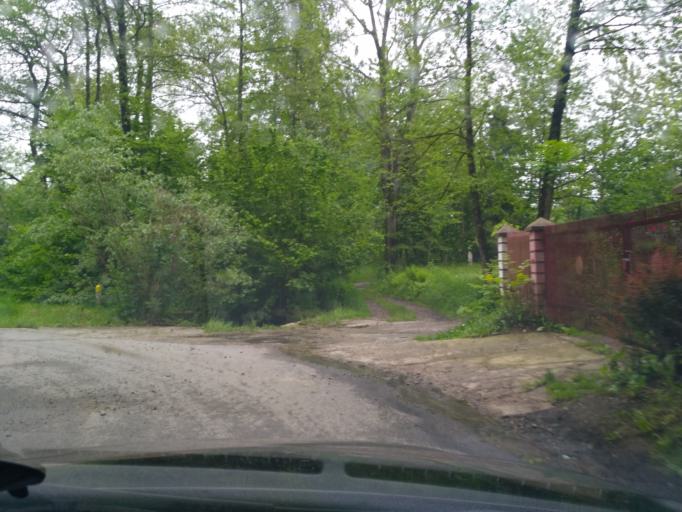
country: PL
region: Subcarpathian Voivodeship
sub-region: Powiat debicki
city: Jodlowa
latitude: 49.8704
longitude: 21.2428
